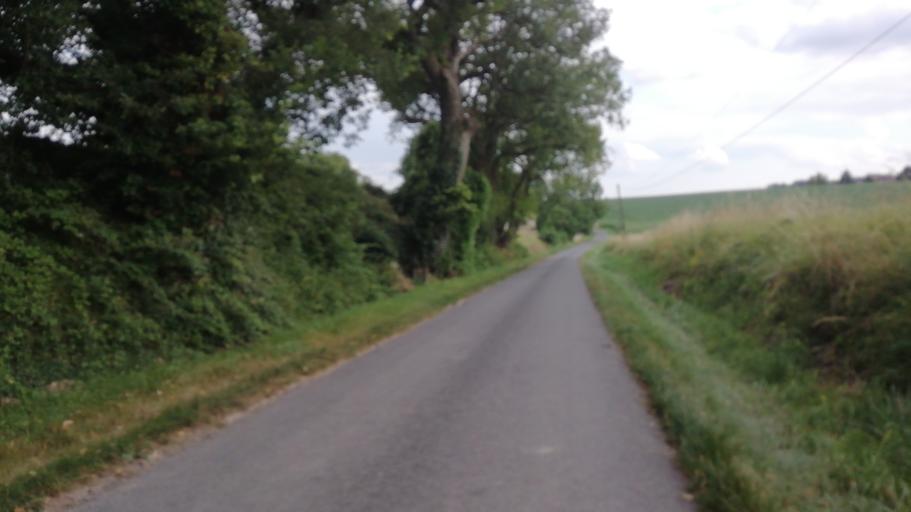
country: FR
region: Poitou-Charentes
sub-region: Departement de la Vienne
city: Thure
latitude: 46.8435
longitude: 0.4559
